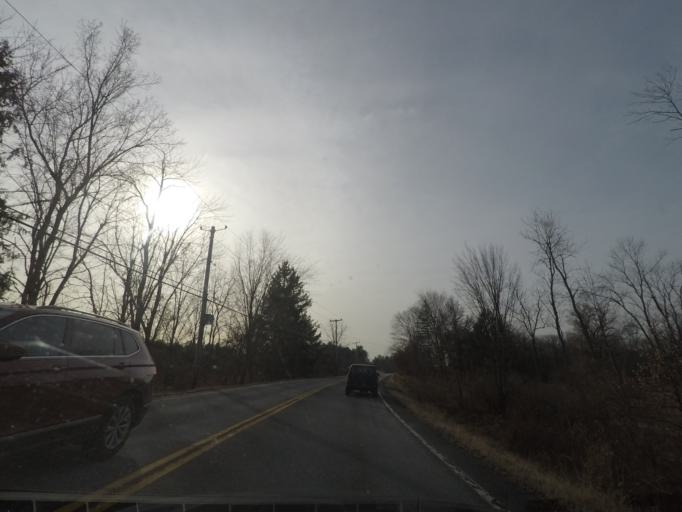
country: US
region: New York
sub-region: Saratoga County
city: Stillwater
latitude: 42.9600
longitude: -73.6339
